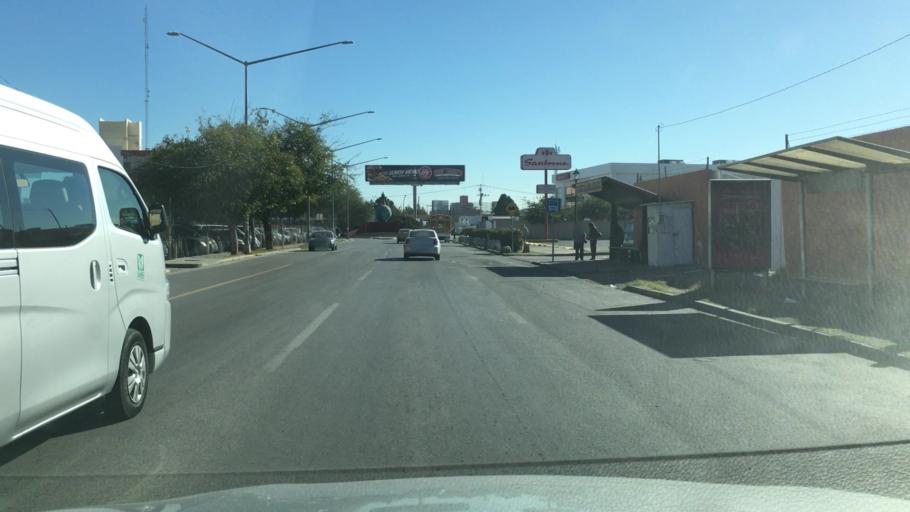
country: MX
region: Chihuahua
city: Ciudad Juarez
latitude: 31.7389
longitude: -106.4511
